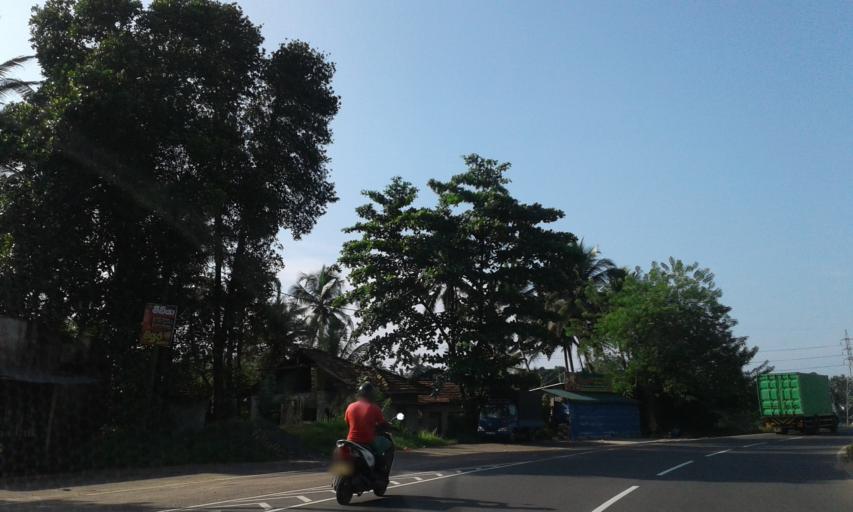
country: LK
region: Western
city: Gampaha
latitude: 7.0556
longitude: 80.0084
